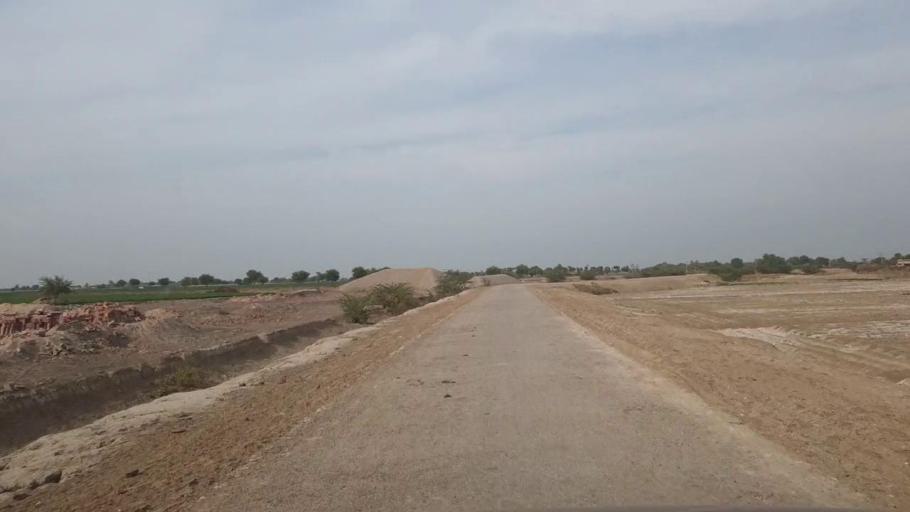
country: PK
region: Sindh
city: Shahpur Chakar
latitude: 26.1028
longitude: 68.5046
